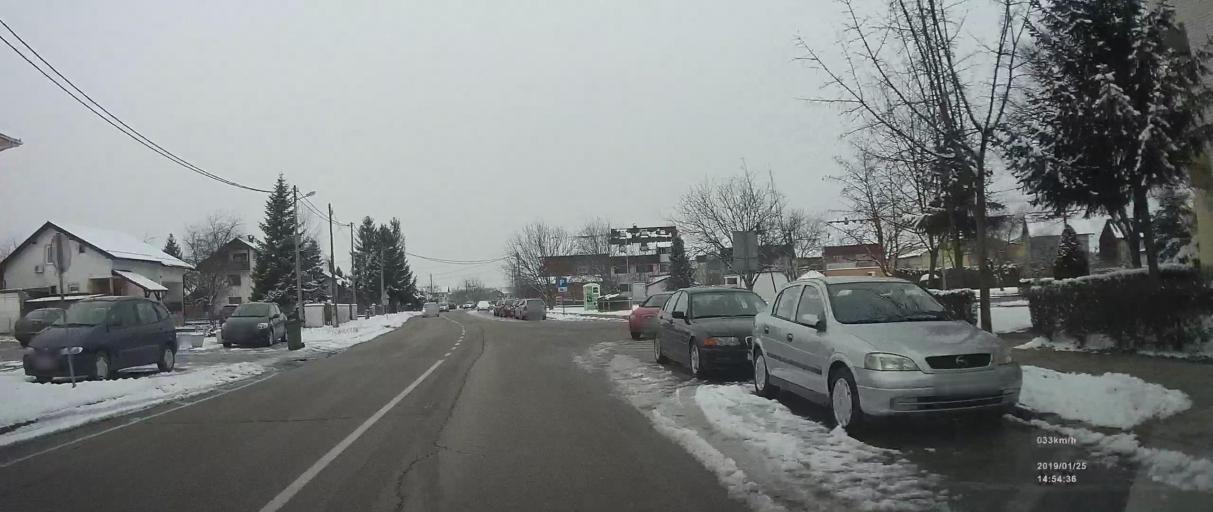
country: HR
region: Zagrebacka
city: Gradici
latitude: 45.7066
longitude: 16.0569
